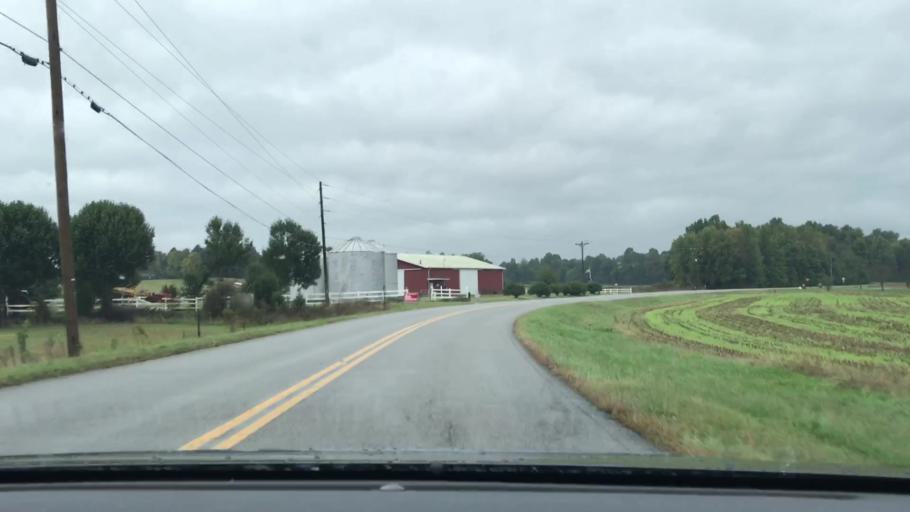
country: US
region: Kentucky
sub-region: McLean County
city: Calhoun
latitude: 37.4534
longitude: -87.2351
